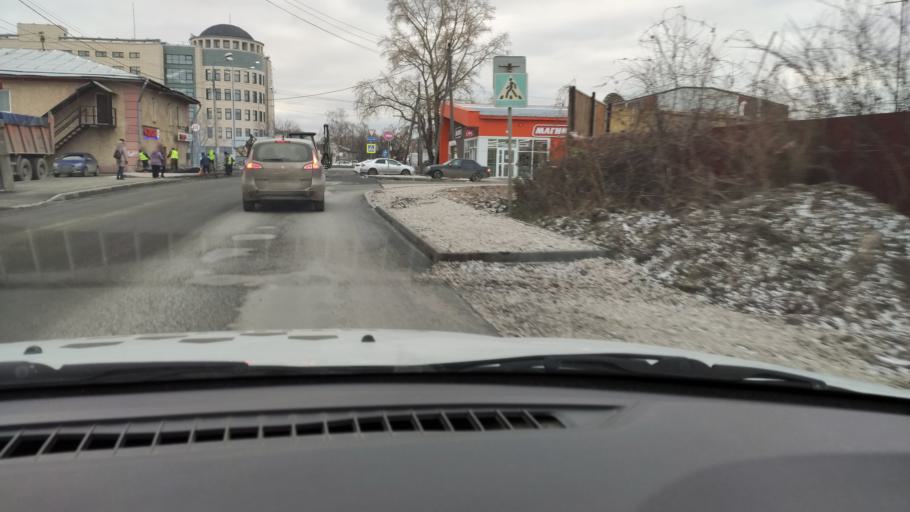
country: RU
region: Perm
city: Kondratovo
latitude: 57.9591
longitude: 56.1283
